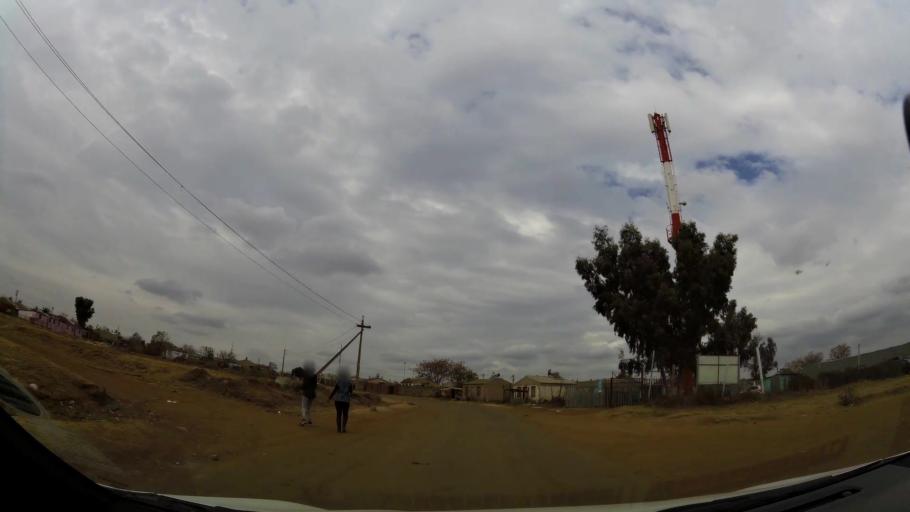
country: ZA
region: Gauteng
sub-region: Ekurhuleni Metropolitan Municipality
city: Germiston
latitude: -26.3913
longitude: 28.1260
